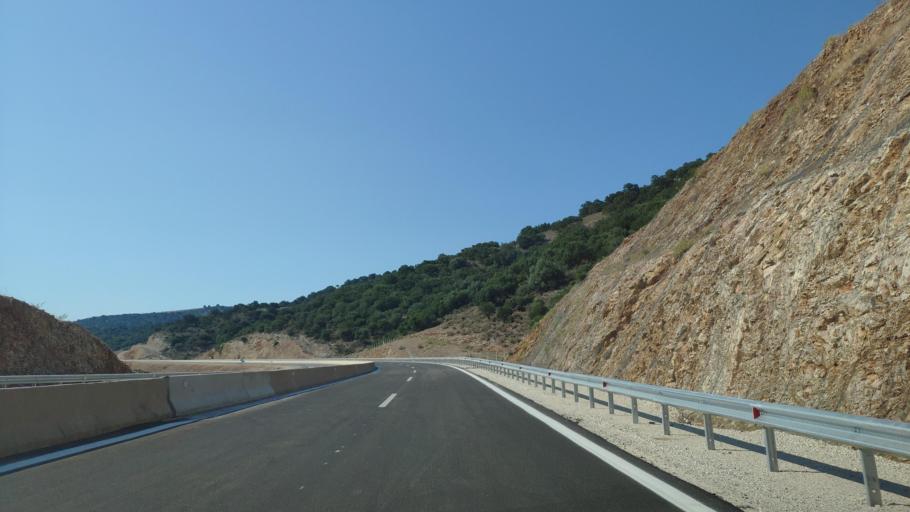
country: GR
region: West Greece
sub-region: Nomos Aitolias kai Akarnanias
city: Katouna
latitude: 38.8344
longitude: 21.1163
